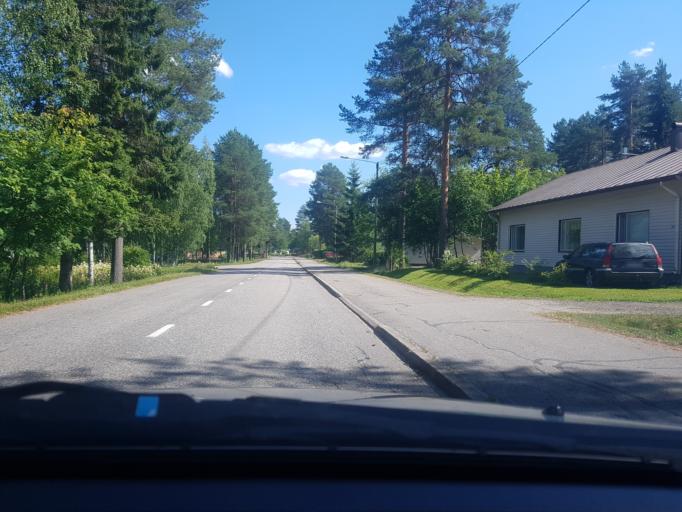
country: FI
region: Kainuu
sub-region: Kehys-Kainuu
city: Kuhmo
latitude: 64.1217
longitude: 29.5244
